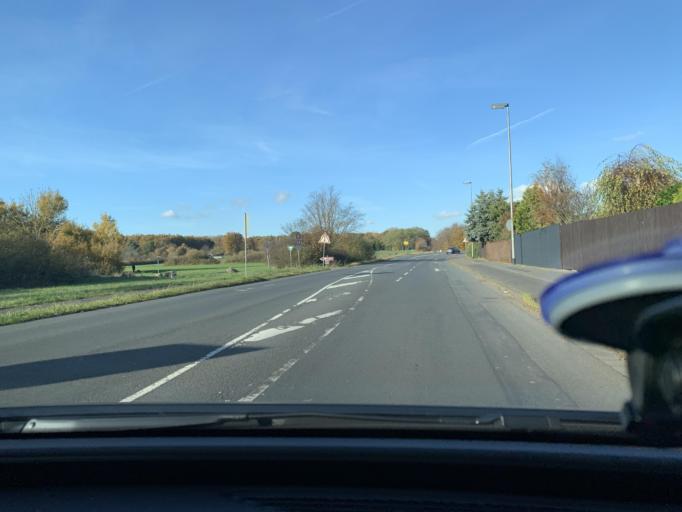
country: DE
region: Hesse
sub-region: Regierungsbezirk Darmstadt
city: Dietzenbach
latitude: 50.0191
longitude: 8.7716
